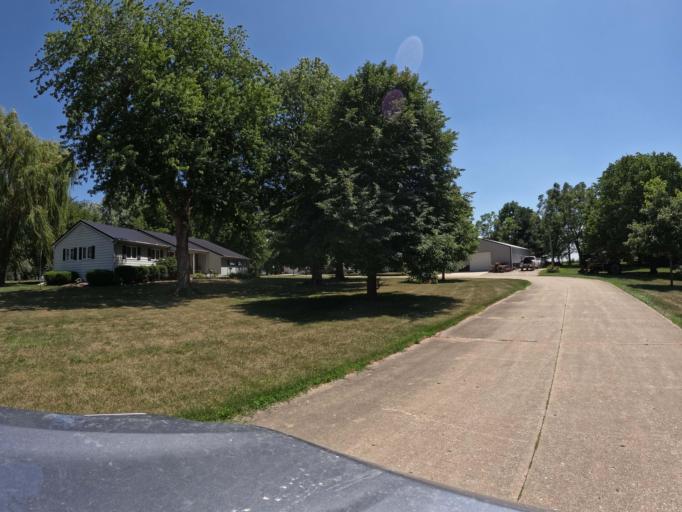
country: US
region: Iowa
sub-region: Poweshiek County
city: Montezuma
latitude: 41.4800
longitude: -92.3905
